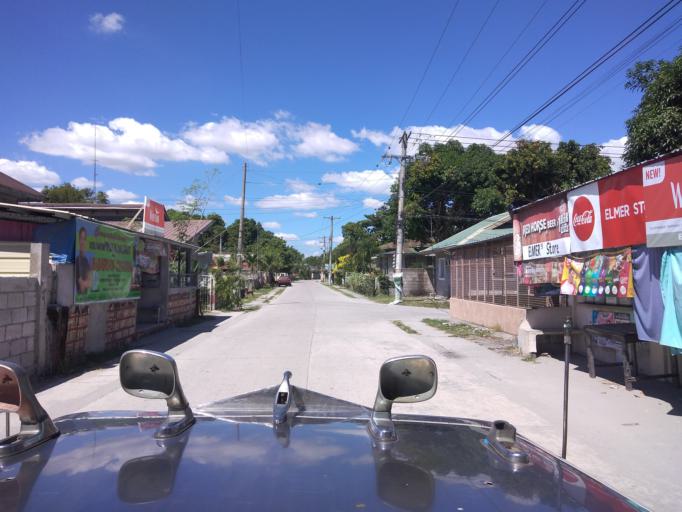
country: PH
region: Central Luzon
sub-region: Province of Pampanga
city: Magliman
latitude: 15.0343
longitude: 120.6479
